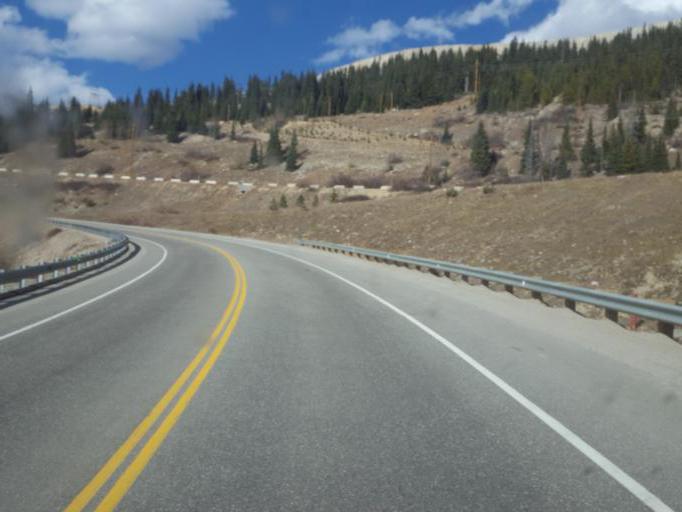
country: US
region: Colorado
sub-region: Lake County
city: Leadville
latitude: 39.3610
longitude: -106.1788
